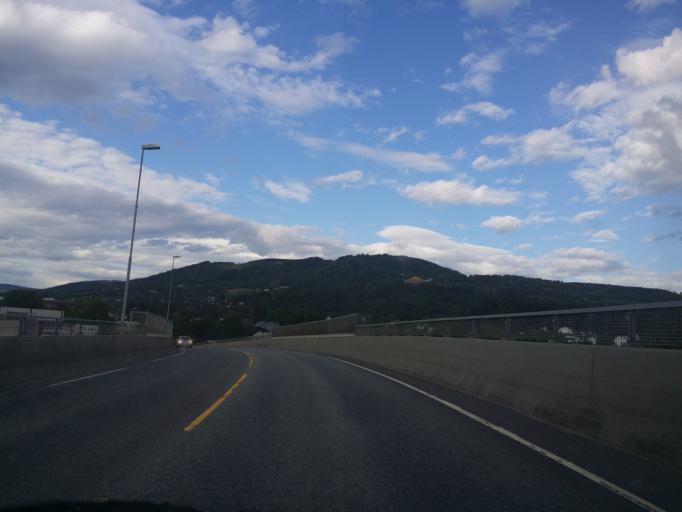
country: NO
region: Hedmark
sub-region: Ringsaker
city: Brumunddal
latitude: 60.8811
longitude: 10.9349
